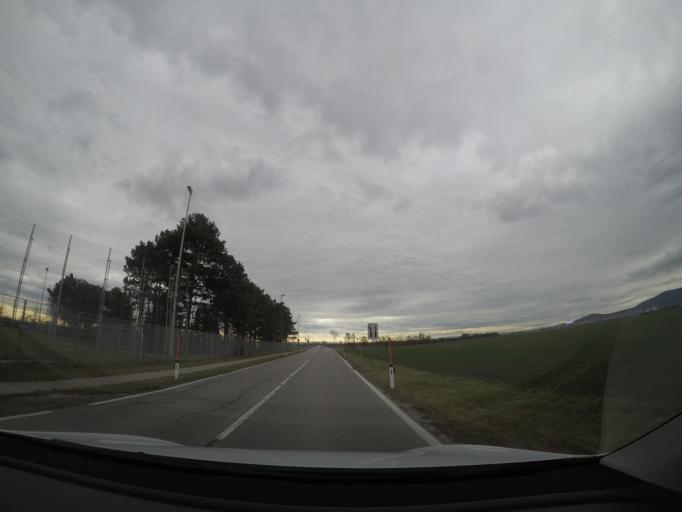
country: AT
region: Lower Austria
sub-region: Politischer Bezirk Modling
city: Vosendorf
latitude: 48.1143
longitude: 16.3344
